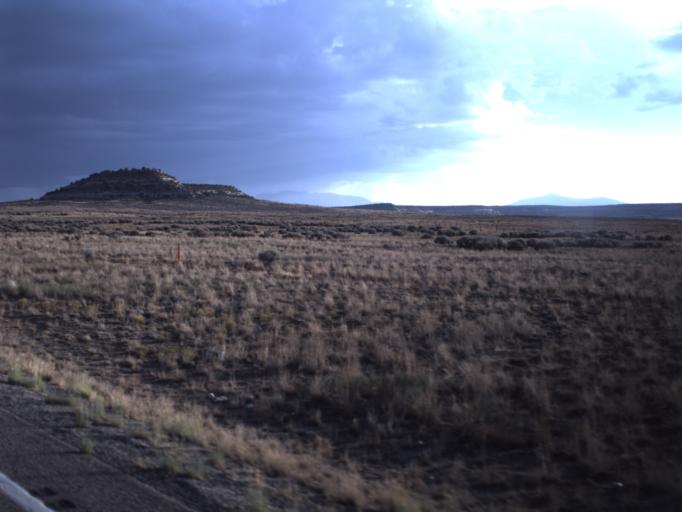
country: US
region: Utah
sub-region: San Juan County
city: Monticello
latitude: 38.1106
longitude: -109.3642
